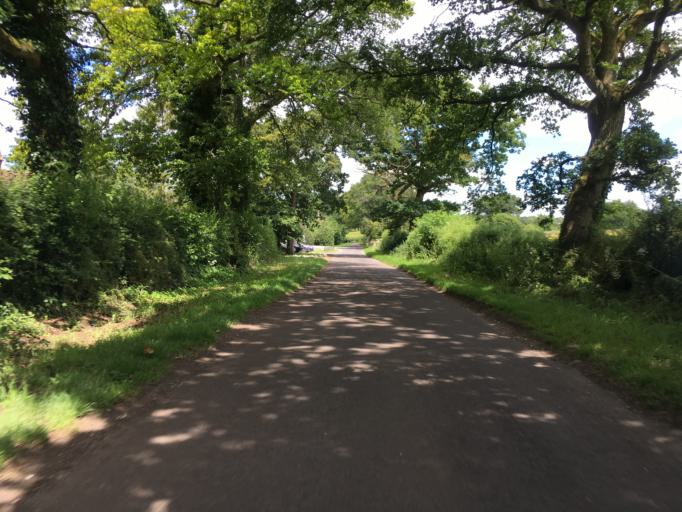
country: GB
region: England
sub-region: Hampshire
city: Highclere
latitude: 51.2833
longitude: -1.4167
